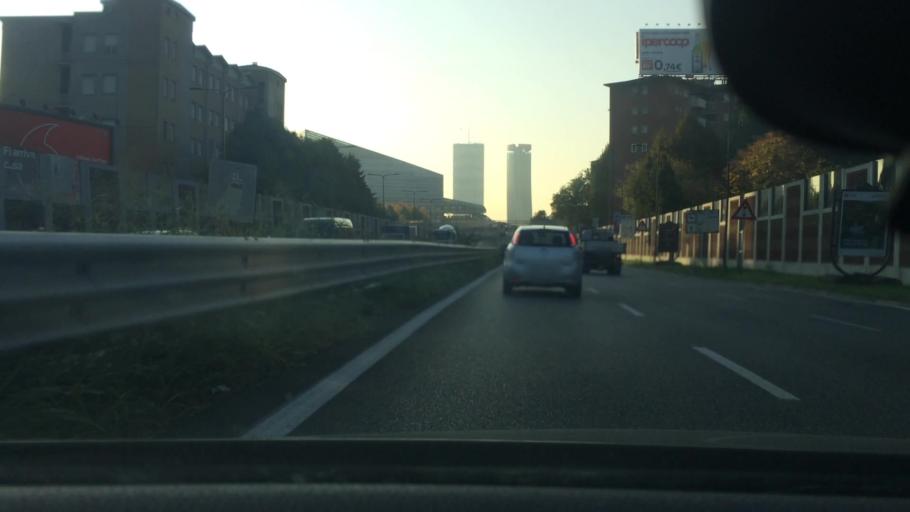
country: IT
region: Lombardy
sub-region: Citta metropolitana di Milano
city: Novate Milanese
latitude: 45.4882
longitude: 9.1414
